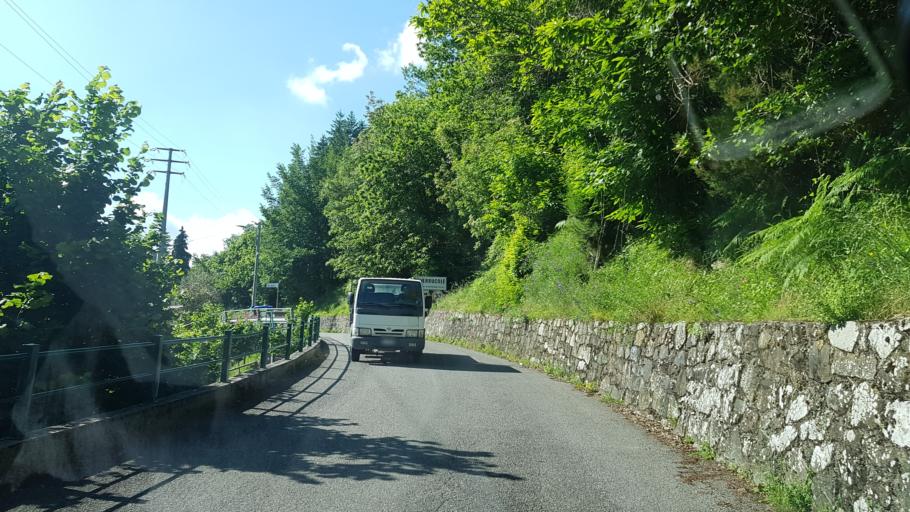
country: IT
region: Tuscany
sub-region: Provincia di Lucca
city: San Romano
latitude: 44.1789
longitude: 10.3382
